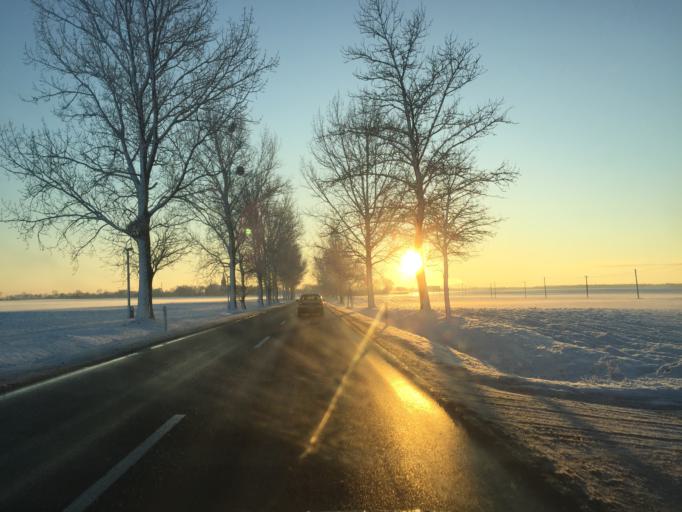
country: PL
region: Kujawsko-Pomorskie
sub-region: Powiat golubsko-dobrzynski
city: Kowalewo Pomorskie
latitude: 53.1263
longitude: 18.8396
